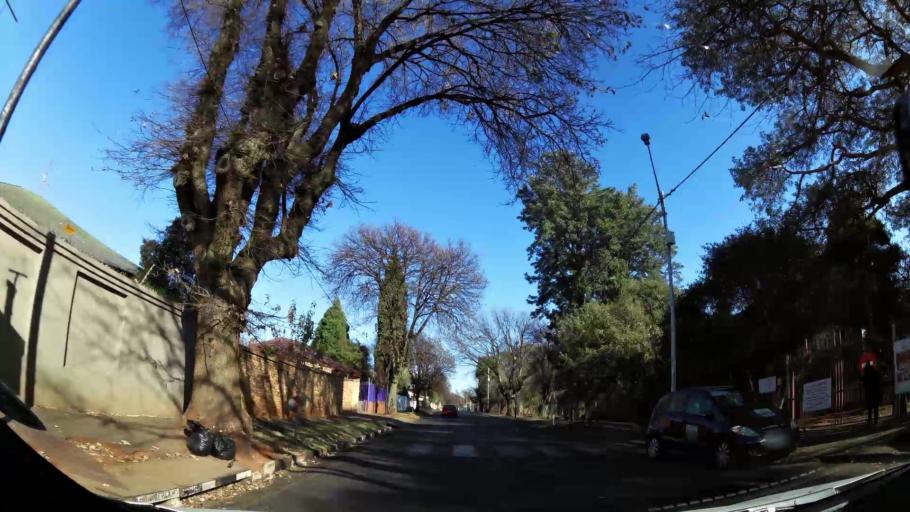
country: ZA
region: Gauteng
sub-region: City of Johannesburg Metropolitan Municipality
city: Johannesburg
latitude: -26.1914
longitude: 28.0937
